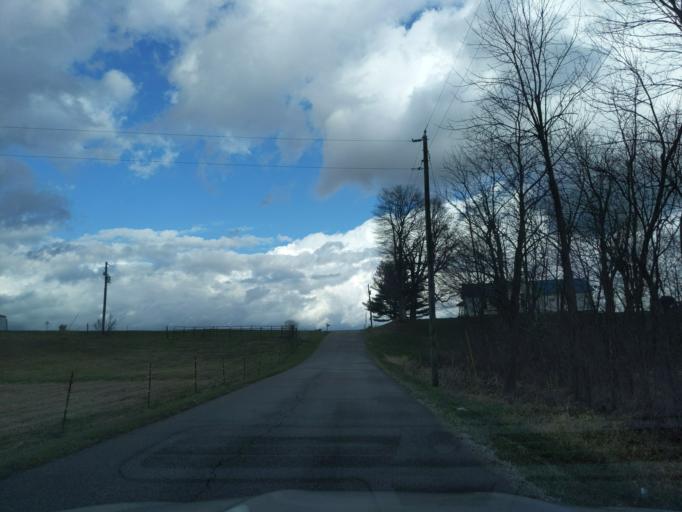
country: US
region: Indiana
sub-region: Decatur County
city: Saint Paul
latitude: 39.3940
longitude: -85.5599
